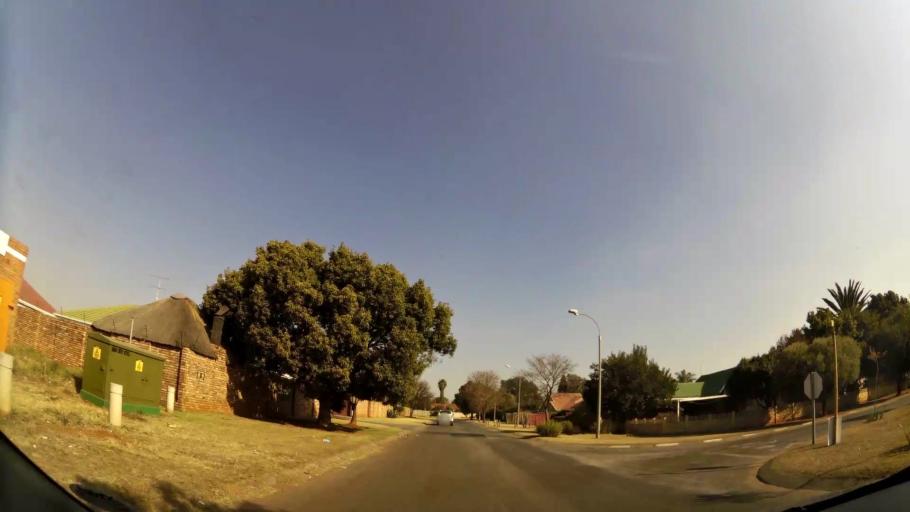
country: ZA
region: Gauteng
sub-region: West Rand District Municipality
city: Randfontein
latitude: -26.1773
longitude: 27.6918
